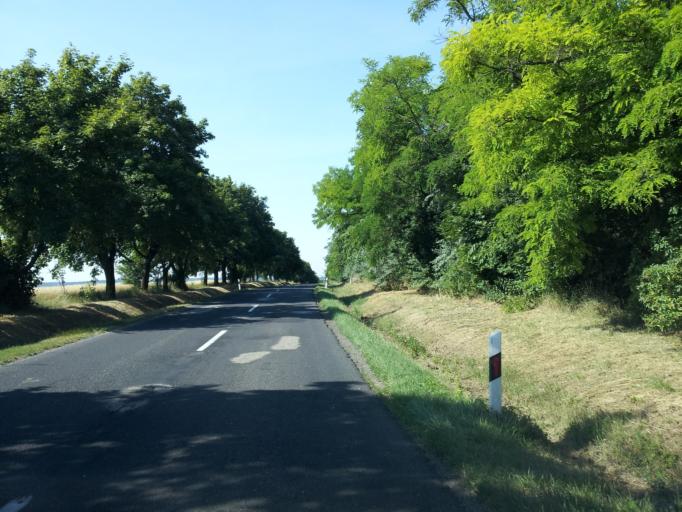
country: HU
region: Fejer
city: Lovasbereny
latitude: 47.3201
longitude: 18.5688
